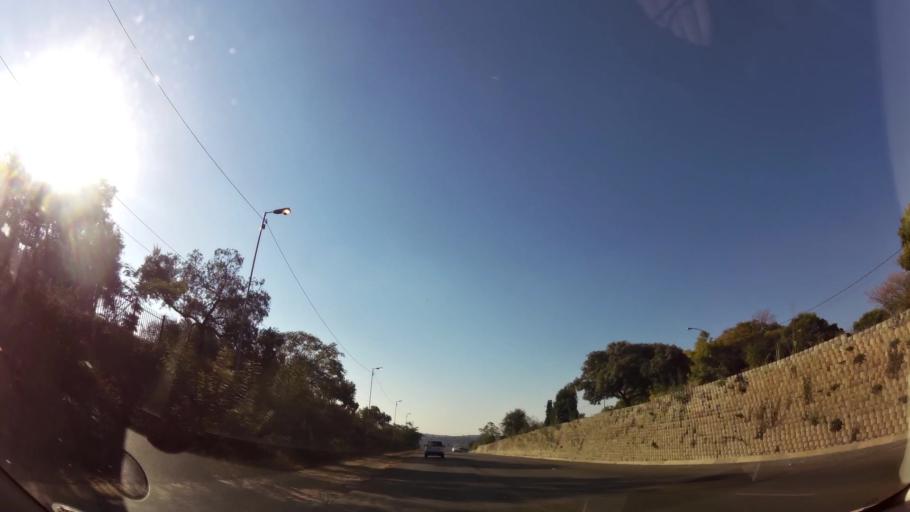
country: ZA
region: Gauteng
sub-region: City of Tshwane Metropolitan Municipality
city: Centurion
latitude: -25.8437
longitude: 28.1533
